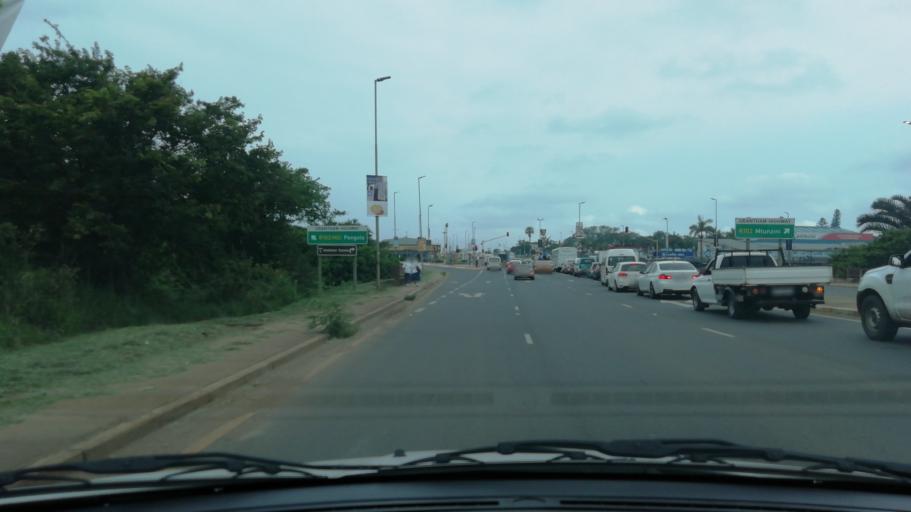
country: ZA
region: KwaZulu-Natal
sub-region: uThungulu District Municipality
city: Empangeni
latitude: -28.7629
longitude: 31.9064
